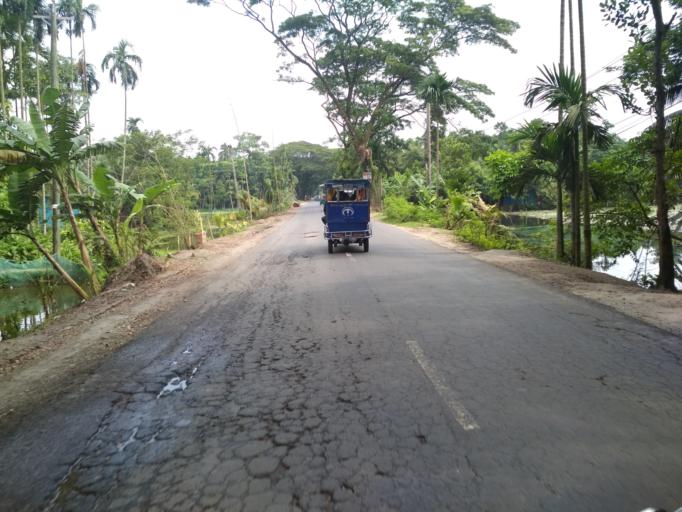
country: BD
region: Chittagong
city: Lakshmipur
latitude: 22.9603
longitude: 90.8095
